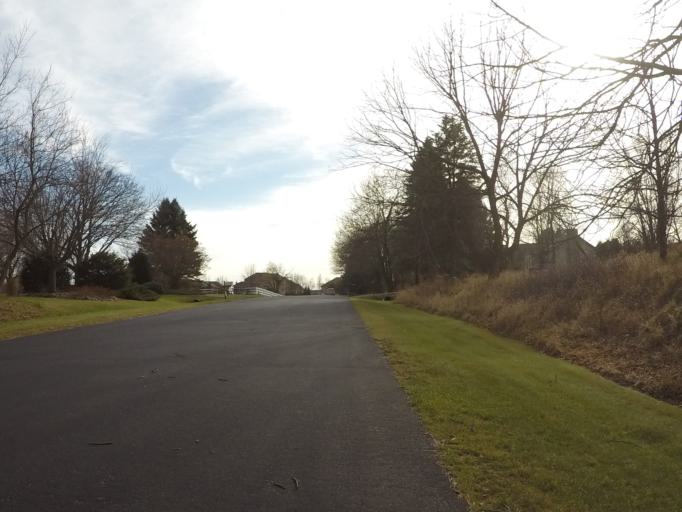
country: US
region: Wisconsin
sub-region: Dane County
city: Middleton
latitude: 43.0838
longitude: -89.5586
